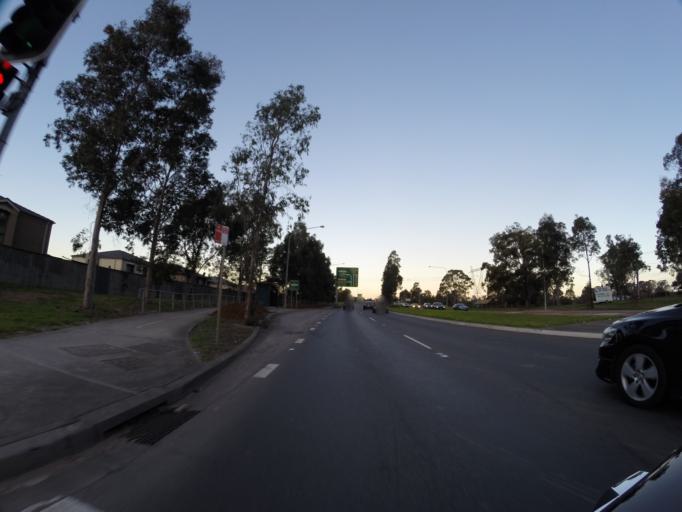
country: AU
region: New South Wales
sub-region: Campbelltown Municipality
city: Glenfield
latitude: -33.9561
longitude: 150.8729
